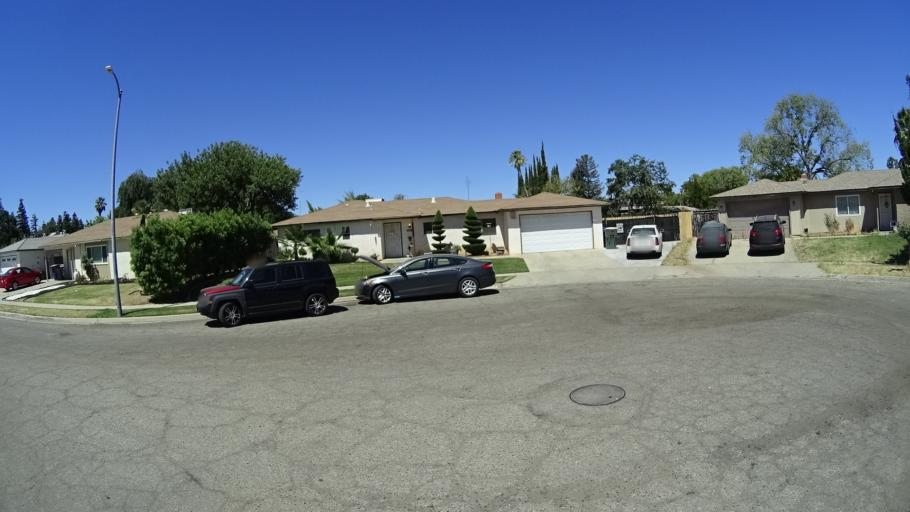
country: US
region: California
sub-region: Fresno County
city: West Park
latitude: 36.7982
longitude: -119.8509
